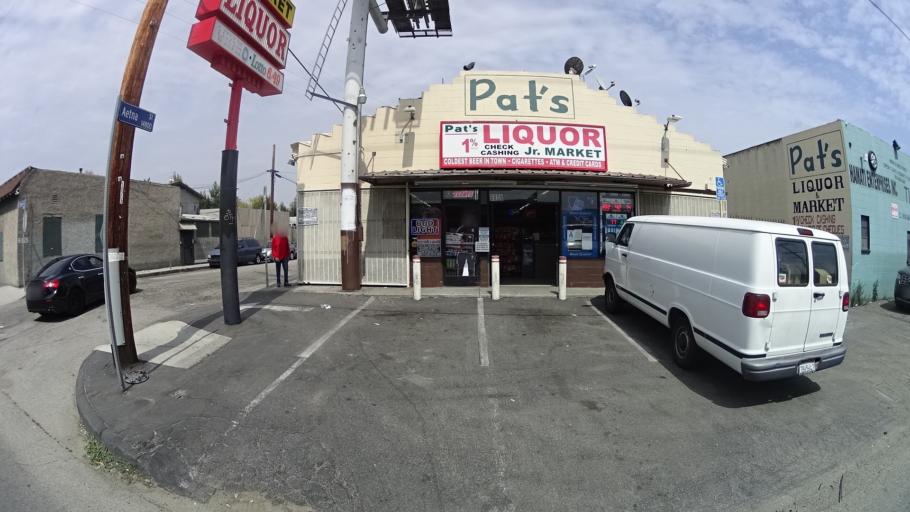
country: US
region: California
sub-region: Los Angeles County
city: Van Nuys
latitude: 34.1800
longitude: -118.4574
